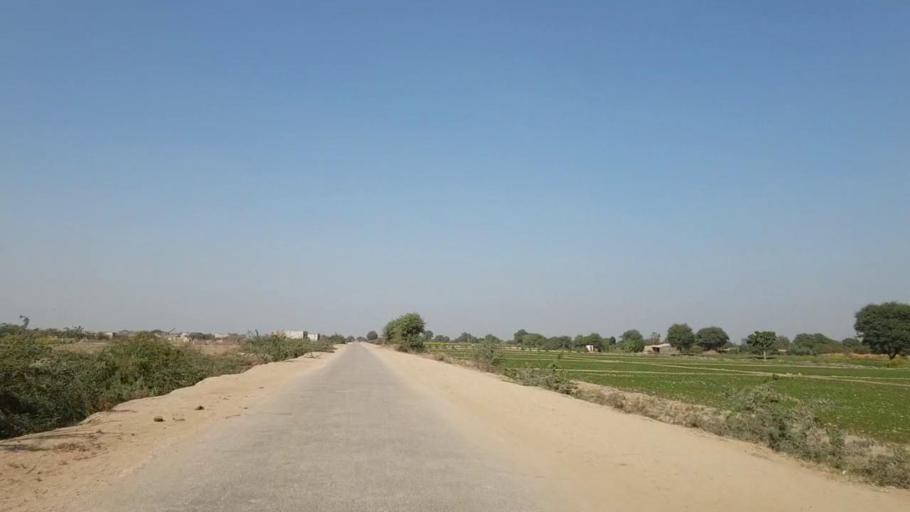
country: PK
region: Sindh
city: Digri
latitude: 25.0105
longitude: 69.1061
